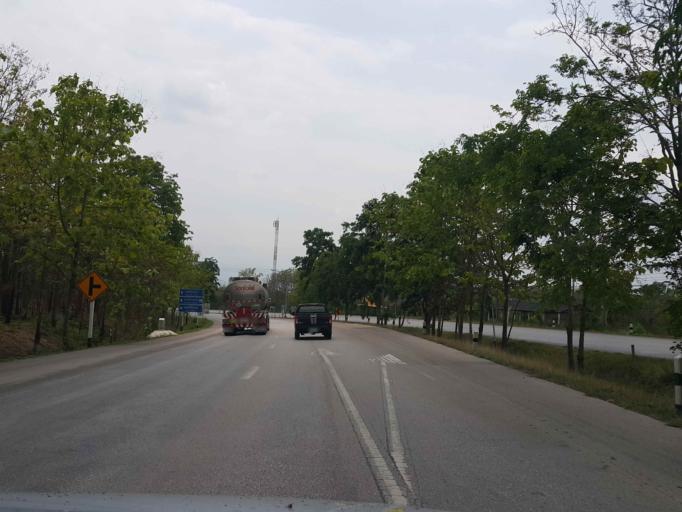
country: TH
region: Lampang
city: Soem Ngam
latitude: 18.0135
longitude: 99.3592
